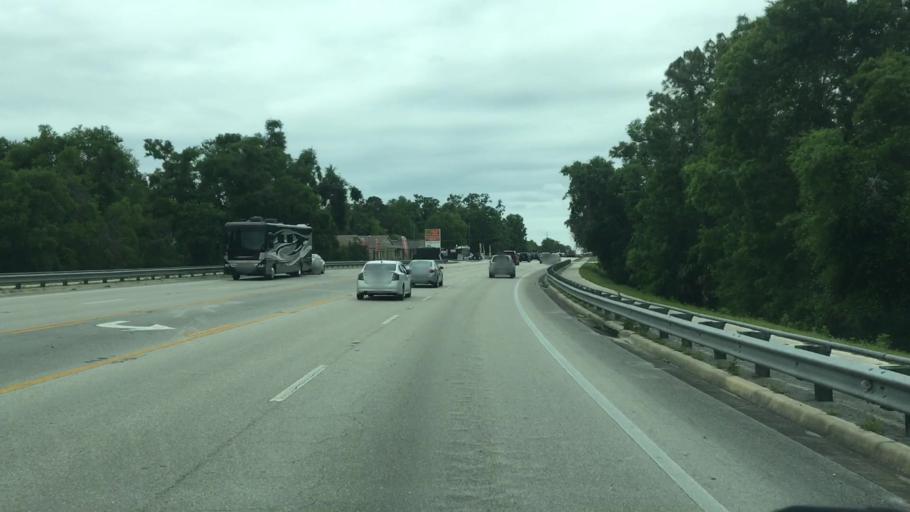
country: US
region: Florida
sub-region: Volusia County
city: De Land Southwest
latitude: 29.0007
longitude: -81.3134
